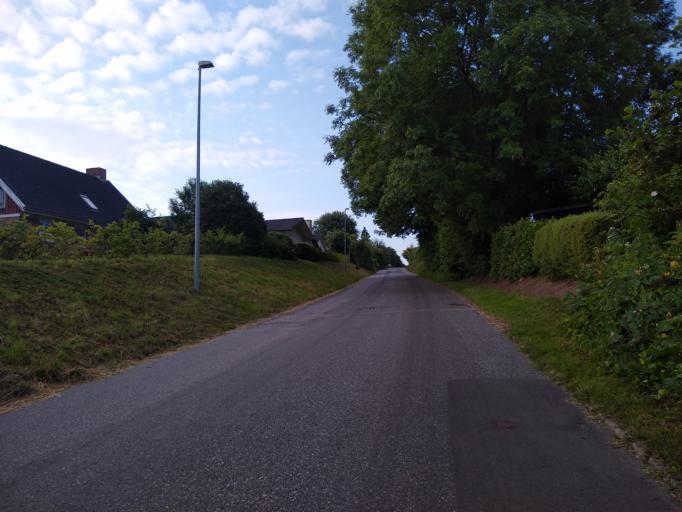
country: DK
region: South Denmark
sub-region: Fredericia Kommune
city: Fredericia
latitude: 55.6195
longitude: 9.7895
